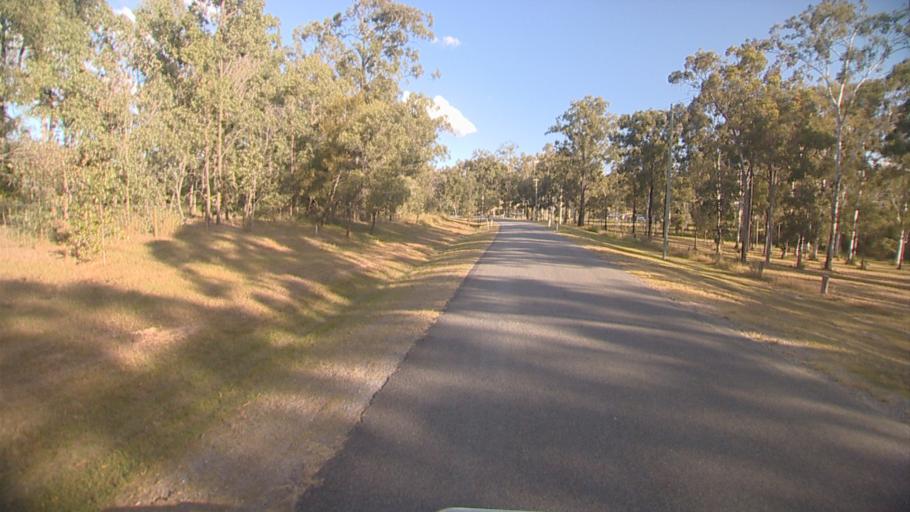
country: AU
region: Queensland
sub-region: Logan
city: North Maclean
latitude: -27.7460
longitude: 152.9409
